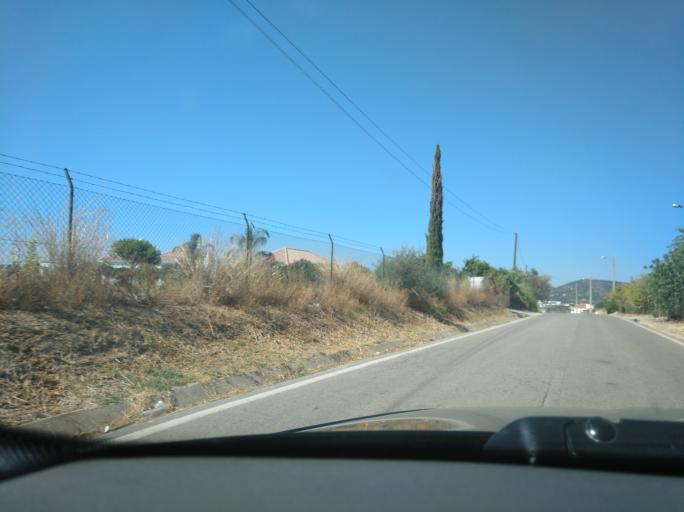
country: PT
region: Faro
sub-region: Faro
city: Faro
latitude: 37.0711
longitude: -7.8949
